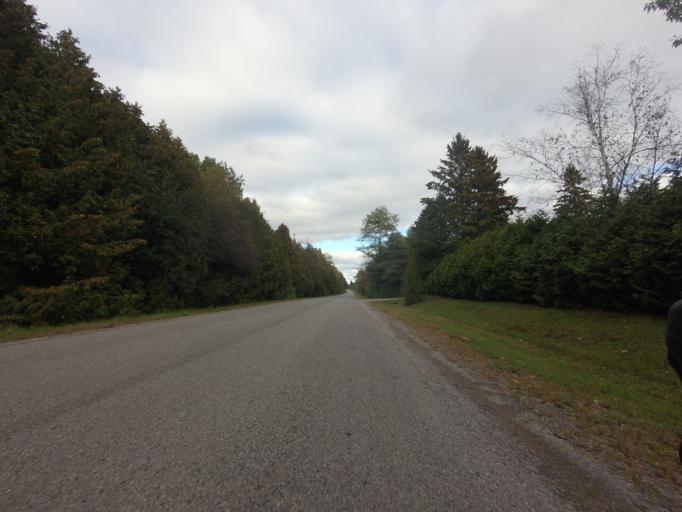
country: CA
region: Ontario
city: Cobourg
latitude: 43.9704
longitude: -78.0413
